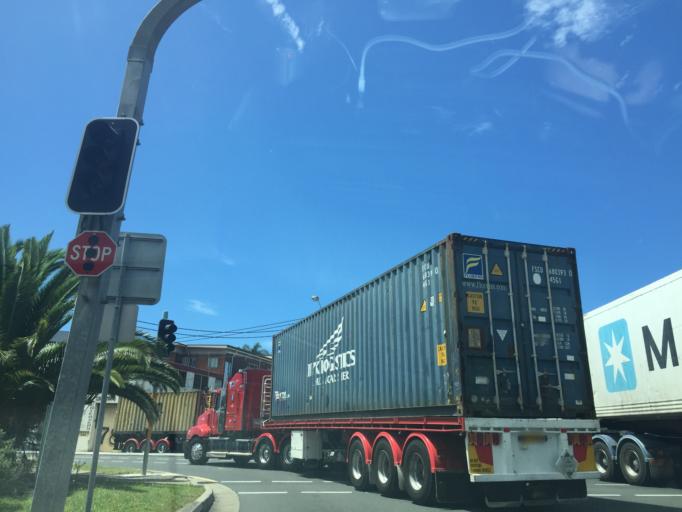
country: AU
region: New South Wales
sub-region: Rockdale
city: Arncliffe
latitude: -33.9363
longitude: 151.1497
